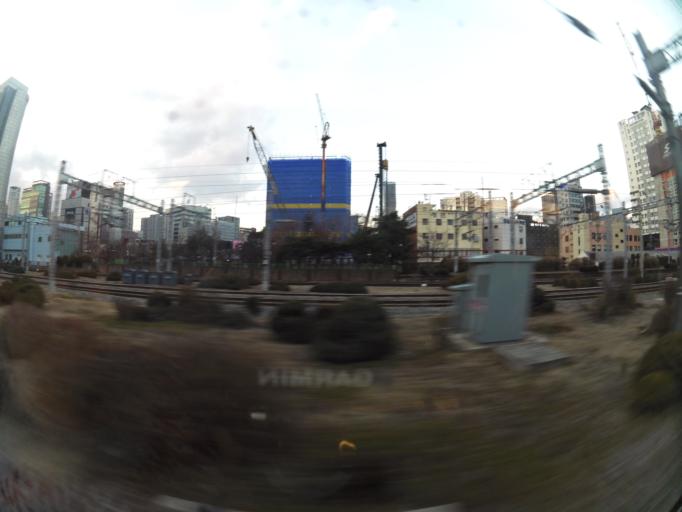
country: KR
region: Gyeonggi-do
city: Kwangmyong
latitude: 37.5164
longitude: 126.9096
